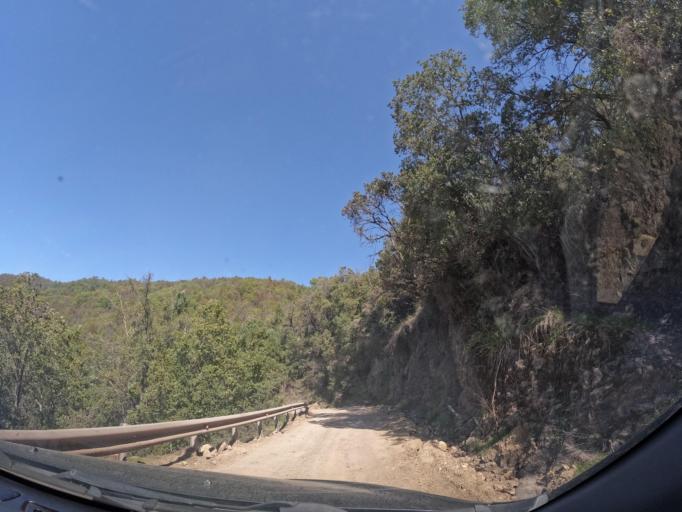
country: CL
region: Maule
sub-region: Provincia de Linares
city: Longavi
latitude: -36.2423
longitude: -71.4408
